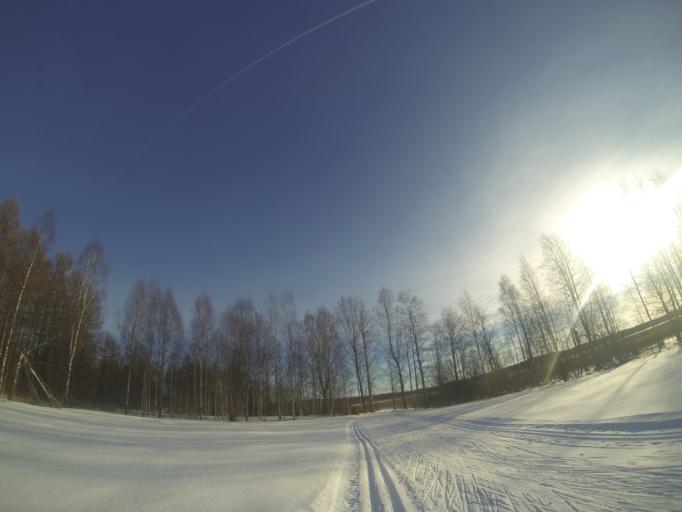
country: FI
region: Southern Savonia
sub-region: Savonlinna
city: Savonlinna
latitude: 61.9140
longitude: 28.9114
